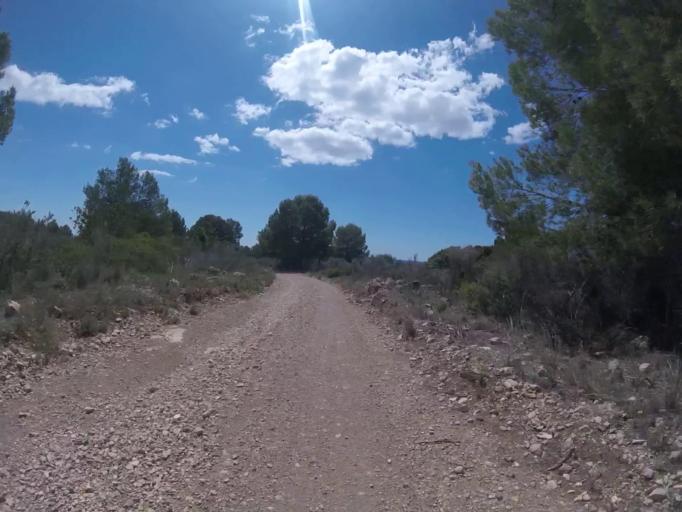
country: ES
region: Valencia
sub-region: Provincia de Castello
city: Alcoceber
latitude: 40.2849
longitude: 0.3234
